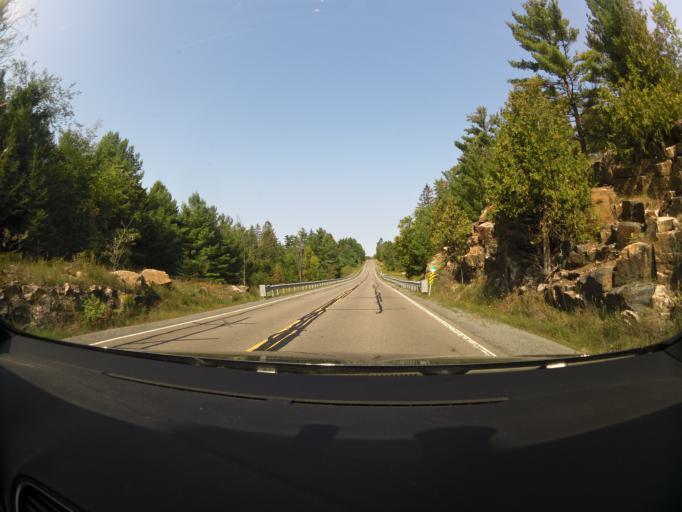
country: CA
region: Ontario
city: Arnprior
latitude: 45.4327
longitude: -76.1705
